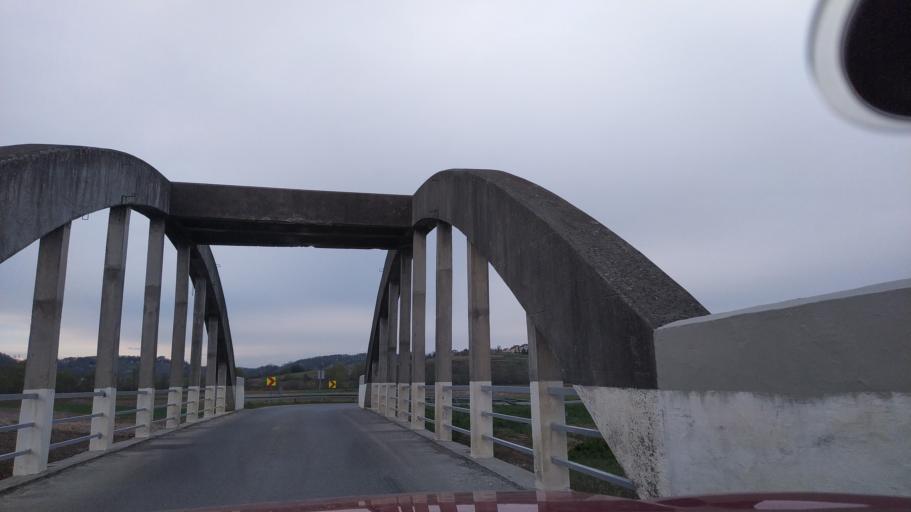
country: HR
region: Varazdinska
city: Jalzabet
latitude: 46.2106
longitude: 16.4629
